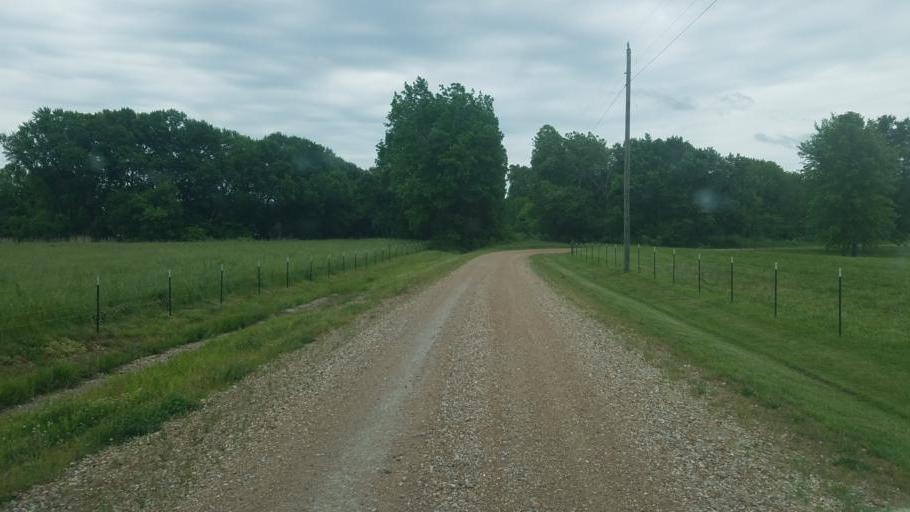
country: US
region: Missouri
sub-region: Moniteau County
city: California
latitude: 38.5943
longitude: -92.6652
